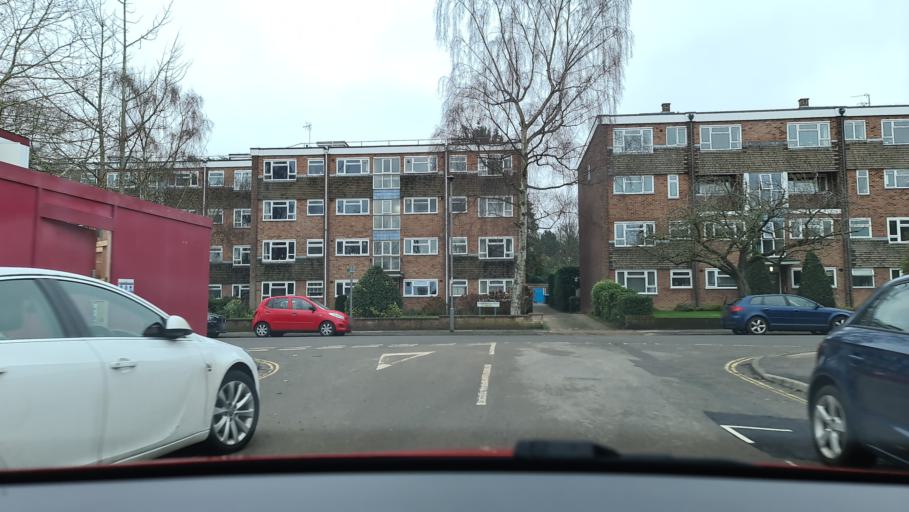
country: GB
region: England
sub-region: Surrey
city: Ditton Hill
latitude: 51.3875
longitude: -0.3106
